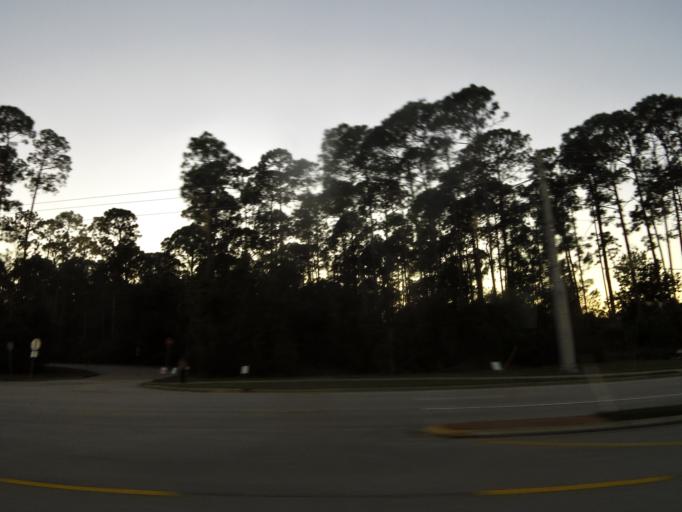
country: US
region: Florida
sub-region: Flagler County
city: Palm Coast
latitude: 29.5555
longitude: -81.2371
